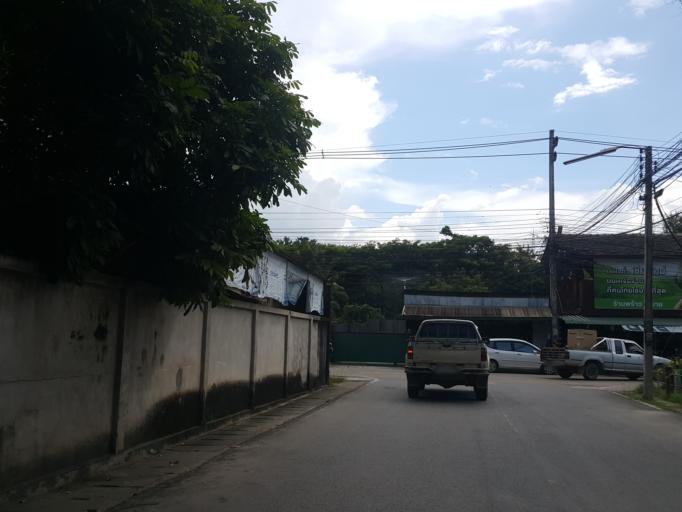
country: TH
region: Chiang Mai
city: Phrao
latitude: 19.3656
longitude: 99.2027
